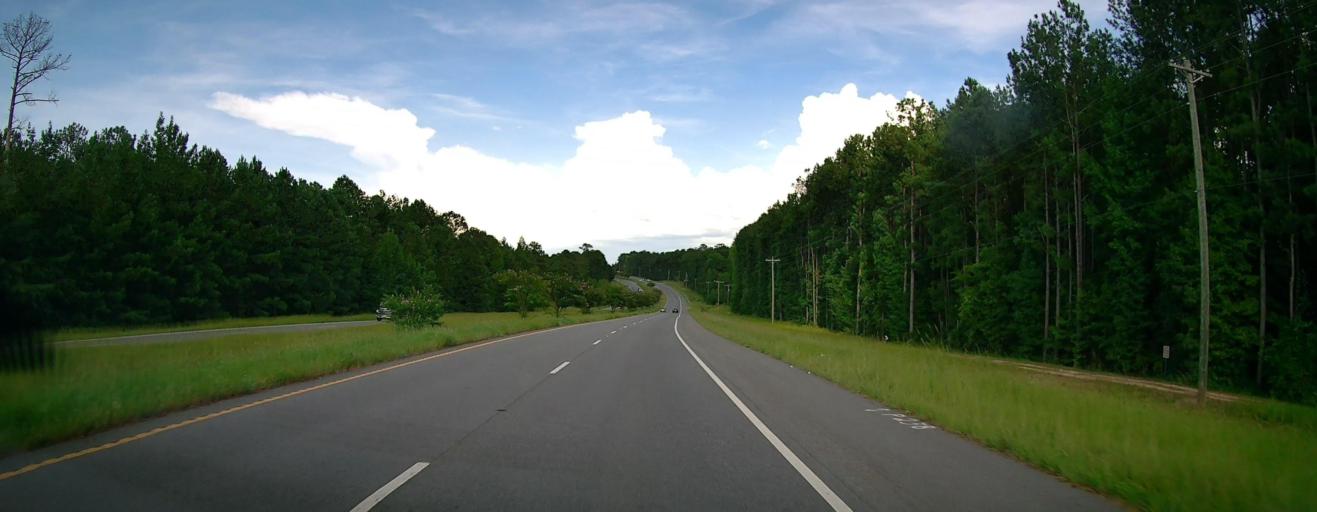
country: US
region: Georgia
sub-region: Talbot County
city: Talbotton
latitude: 32.5494
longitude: -84.6991
